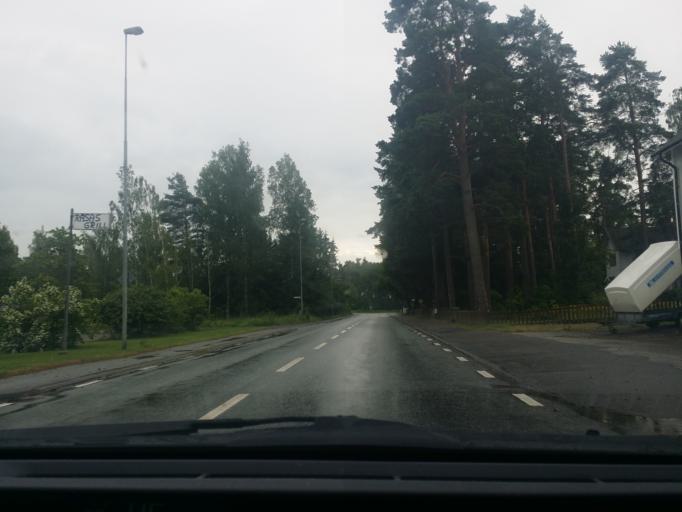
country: SE
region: OErebro
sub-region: Lindesbergs Kommun
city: Fellingsbro
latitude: 59.4305
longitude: 15.5957
